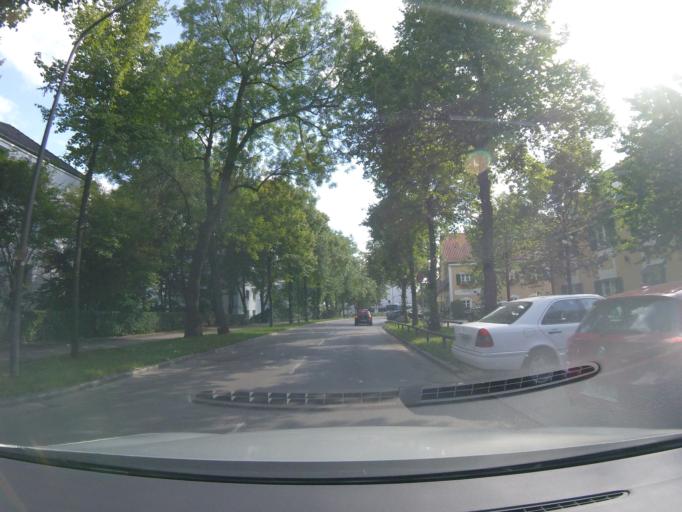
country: DE
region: Bavaria
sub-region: Upper Bavaria
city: Unterfoehring
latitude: 48.1746
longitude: 11.6298
